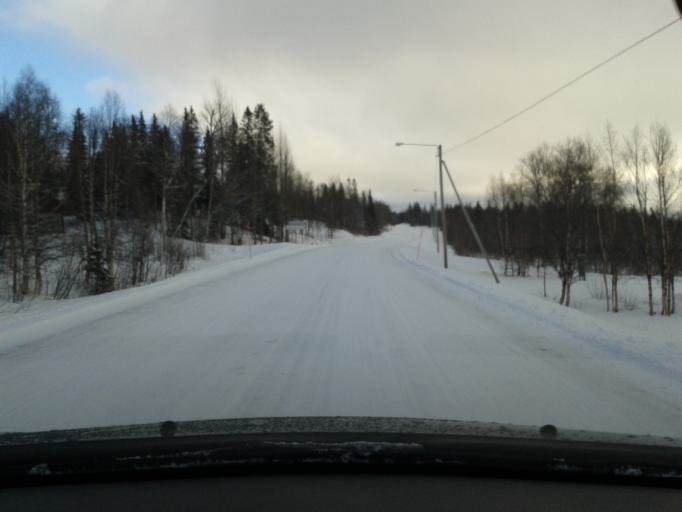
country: SE
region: Vaesterbotten
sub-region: Vilhelmina Kommun
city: Sjoberg
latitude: 65.2507
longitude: 15.5812
